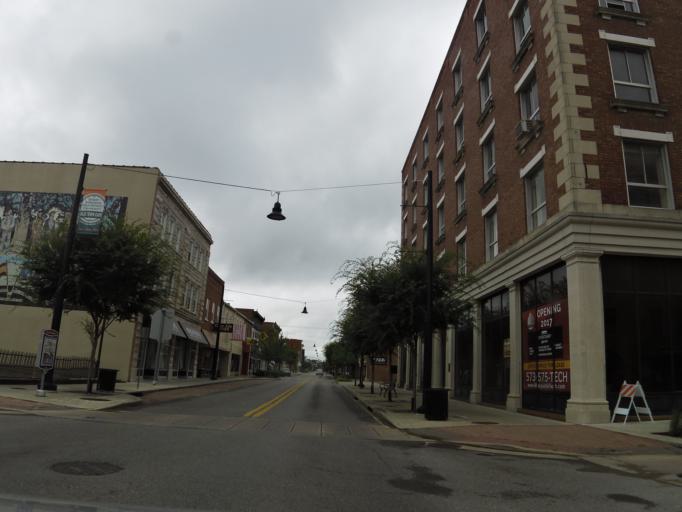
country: US
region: Missouri
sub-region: Cape Girardeau County
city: Cape Girardeau
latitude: 37.3063
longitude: -89.5221
